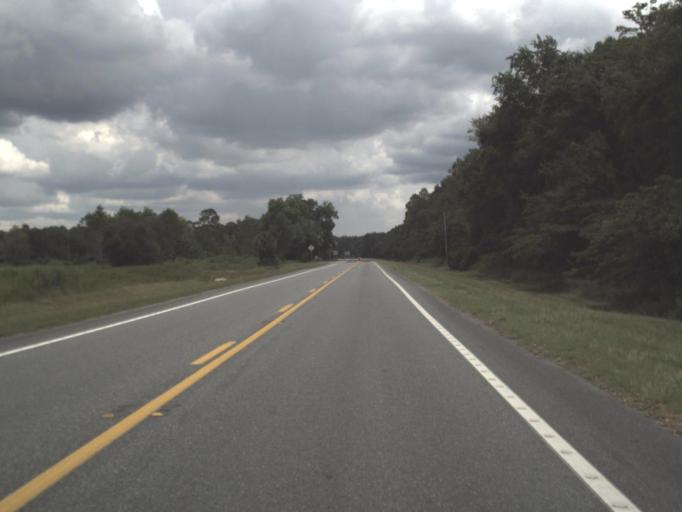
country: US
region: Florida
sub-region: Taylor County
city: Perry
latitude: 30.0811
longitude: -83.5124
